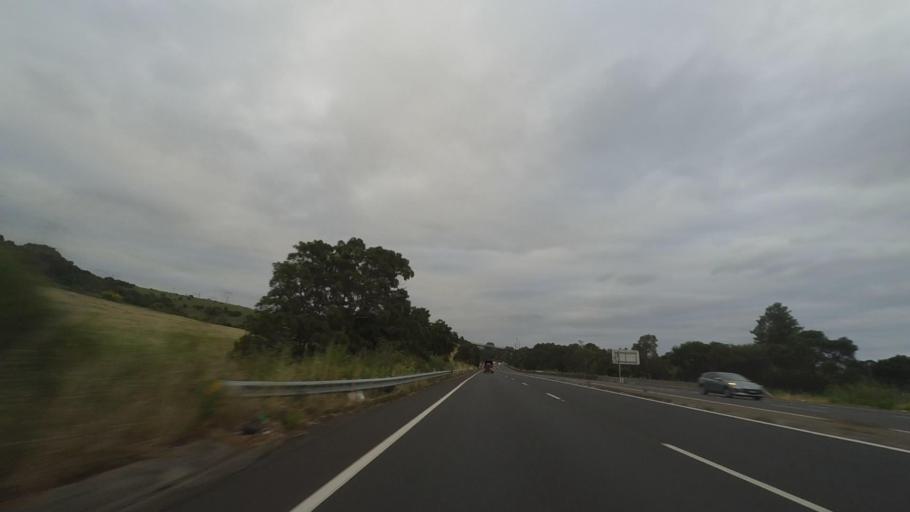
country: AU
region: New South Wales
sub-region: Kiama
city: Kiama
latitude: -34.6856
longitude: 150.8441
